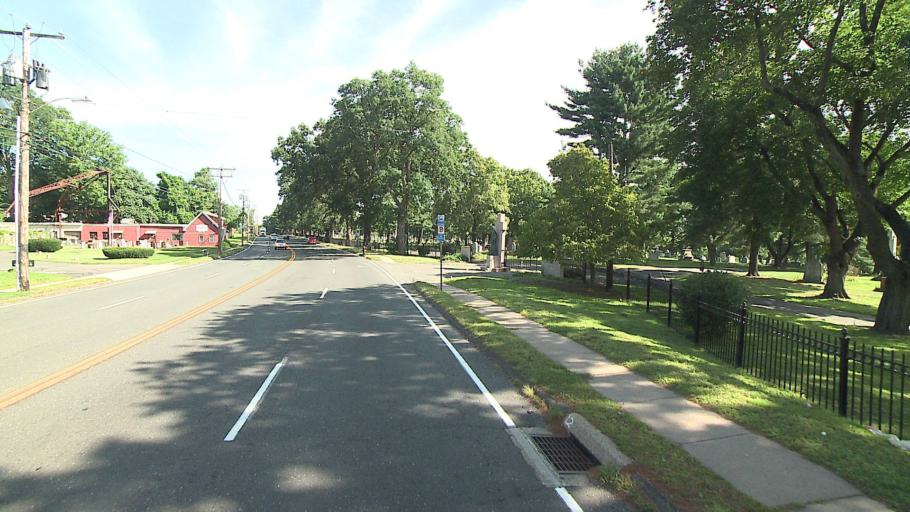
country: US
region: Connecticut
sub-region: Hartford County
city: Blue Hills
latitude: 41.8120
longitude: -72.6948
